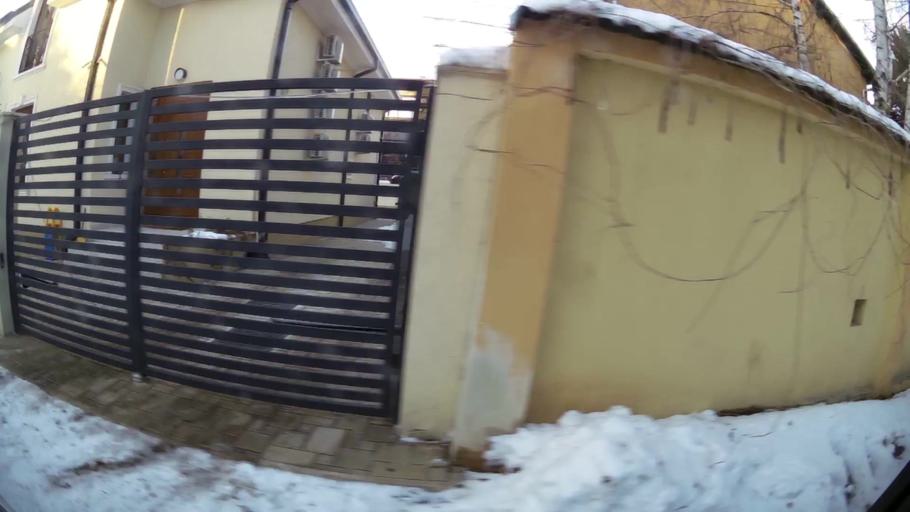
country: RO
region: Ilfov
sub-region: Comuna Popesti-Leordeni
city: Popesti-Leordeni
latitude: 44.3772
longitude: 26.1264
